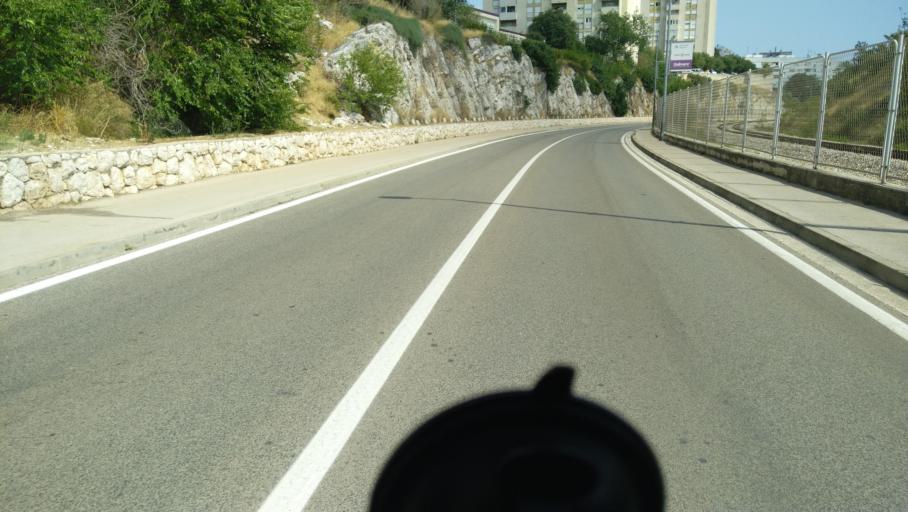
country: HR
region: Sibensko-Kniniska
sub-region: Grad Sibenik
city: Sibenik
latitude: 43.7285
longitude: 15.9018
